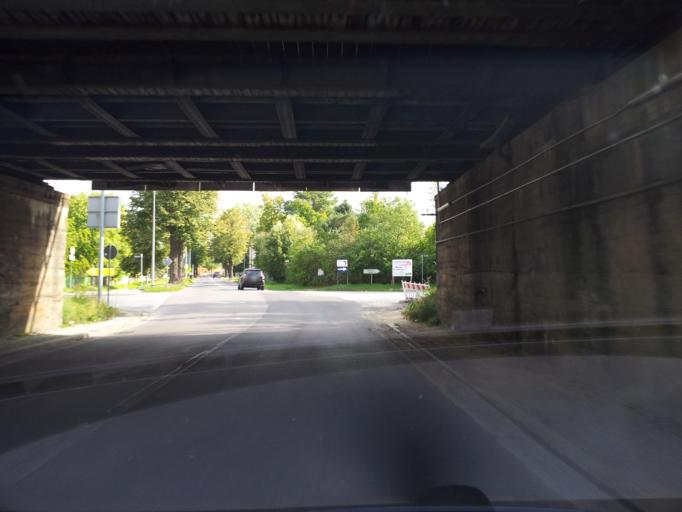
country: DE
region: Brandenburg
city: Ruhland
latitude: 51.4575
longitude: 13.8732
